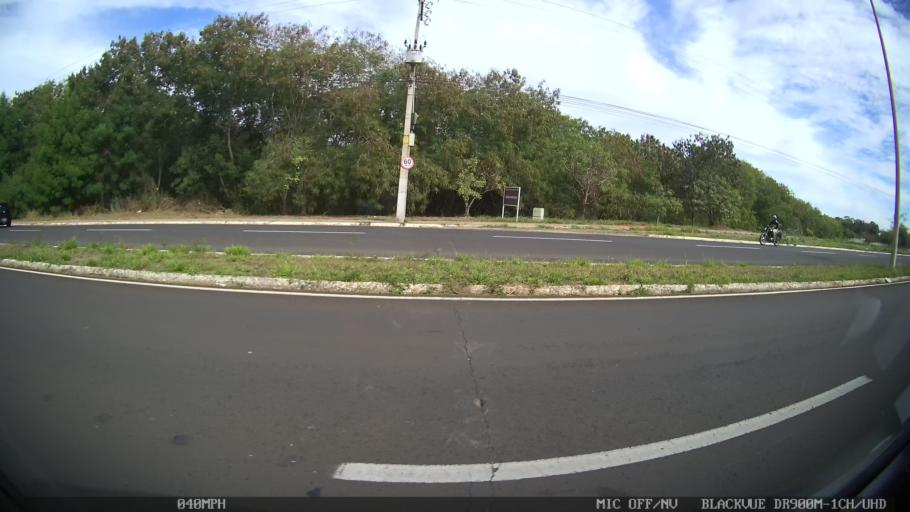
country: BR
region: Sao Paulo
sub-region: Catanduva
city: Catanduva
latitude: -21.1433
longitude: -48.9522
